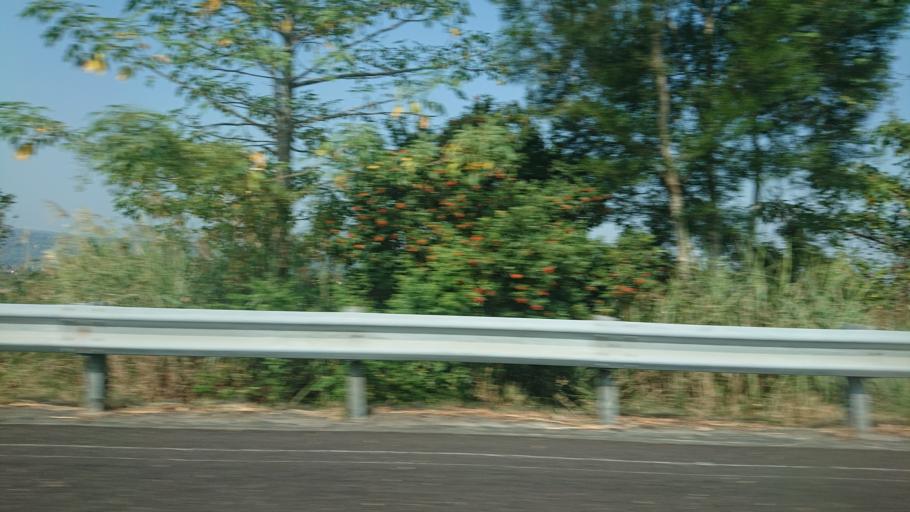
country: TW
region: Taiwan
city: Lugu
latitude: 23.8174
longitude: 120.7025
